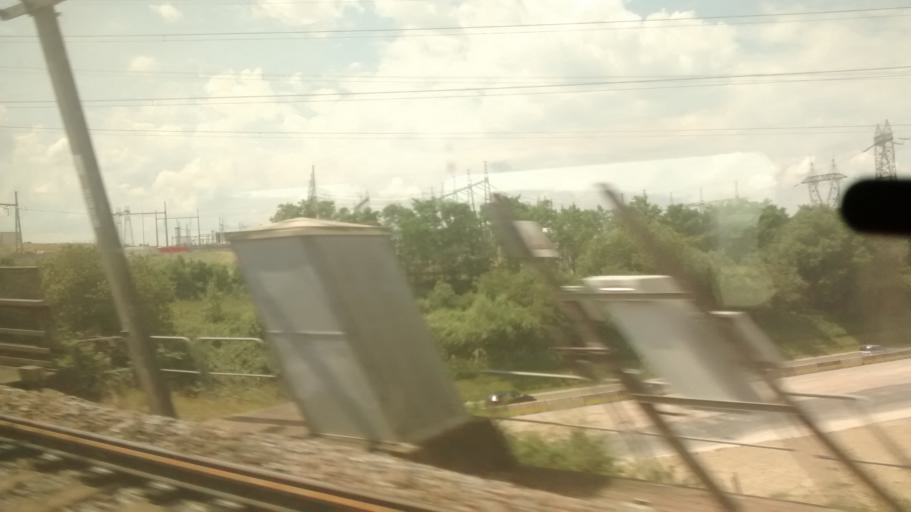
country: FR
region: Bourgogne
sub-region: Departement de Saone-et-Loire
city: Saint-Leu
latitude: 46.7499
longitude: 4.5048
